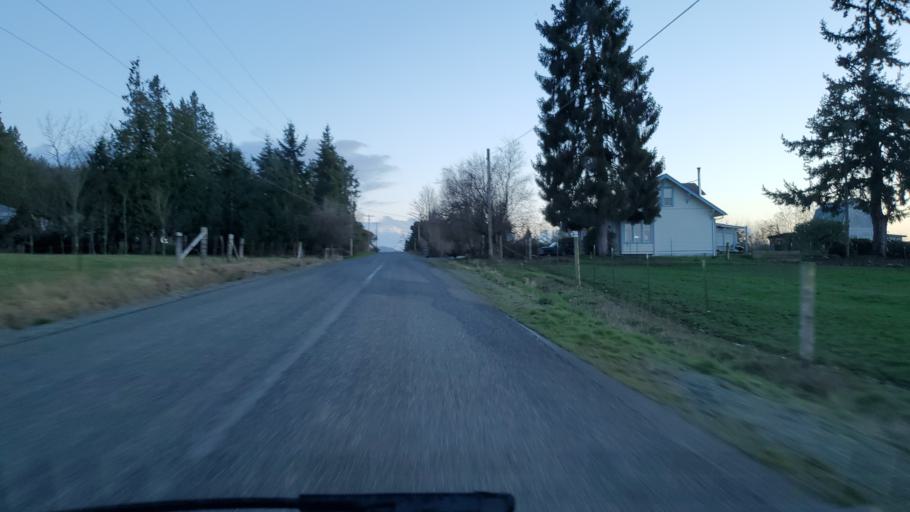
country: US
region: Washington
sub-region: Skagit County
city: Burlington
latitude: 48.4581
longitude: -122.2920
